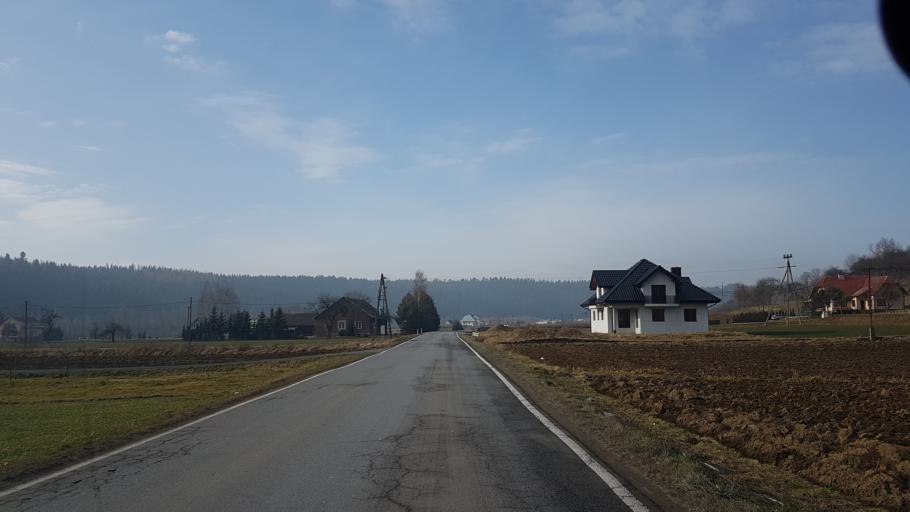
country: PL
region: Lesser Poland Voivodeship
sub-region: Powiat nowosadecki
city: Podegrodzie
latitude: 49.5609
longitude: 20.5687
